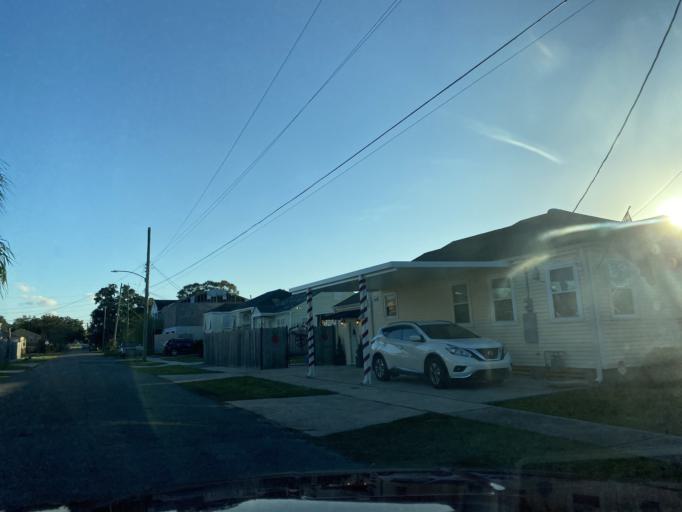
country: US
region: Louisiana
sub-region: Orleans Parish
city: New Orleans
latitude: 30.0193
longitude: -90.0527
